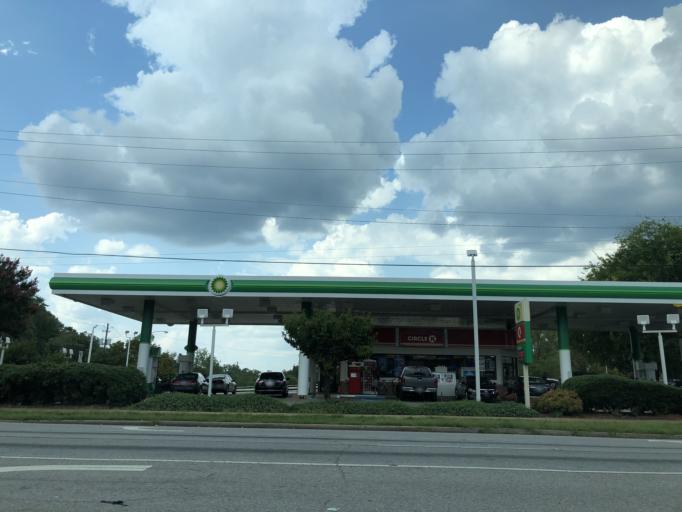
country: US
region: Georgia
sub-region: Clarke County
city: Athens
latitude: 33.9620
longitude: -83.3931
